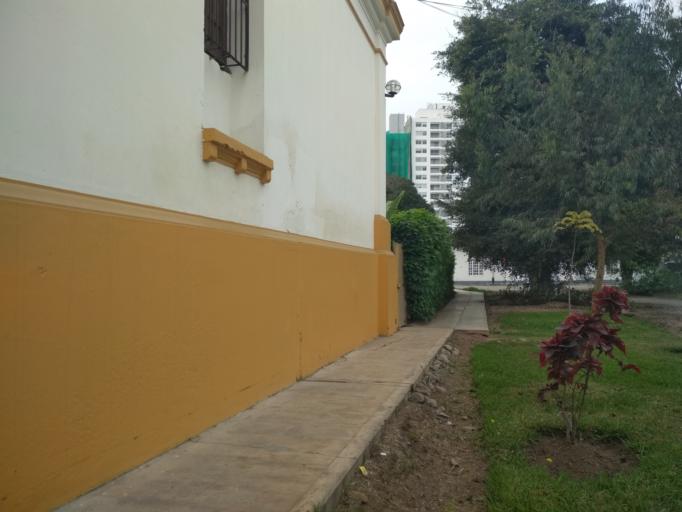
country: PE
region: Lima
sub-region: Lima
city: San Isidro
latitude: -12.0988
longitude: -77.0643
